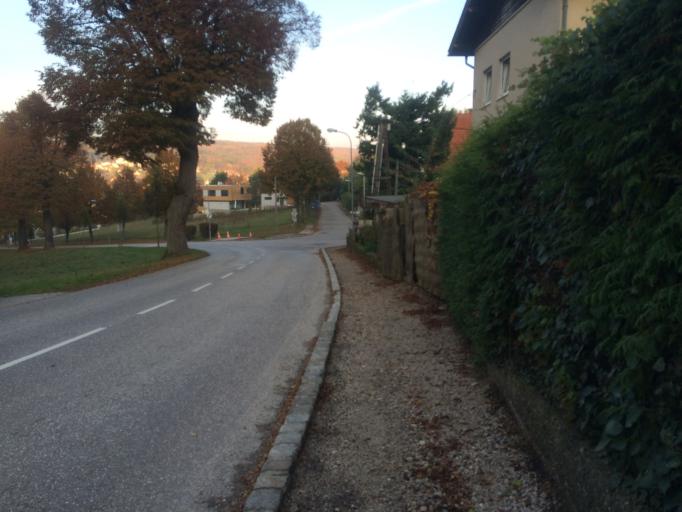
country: AT
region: Lower Austria
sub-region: Politischer Bezirk Wien-Umgebung
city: Gablitz
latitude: 48.2270
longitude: 16.1443
